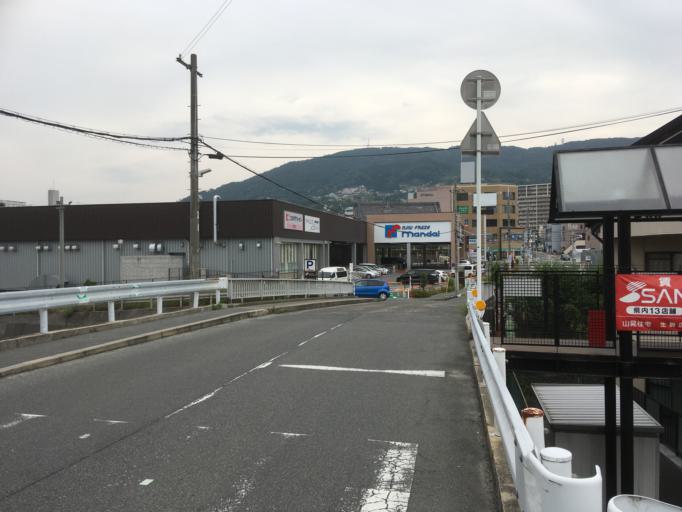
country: JP
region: Nara
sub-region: Ikoma-shi
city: Ikoma
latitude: 34.6964
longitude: 135.7024
